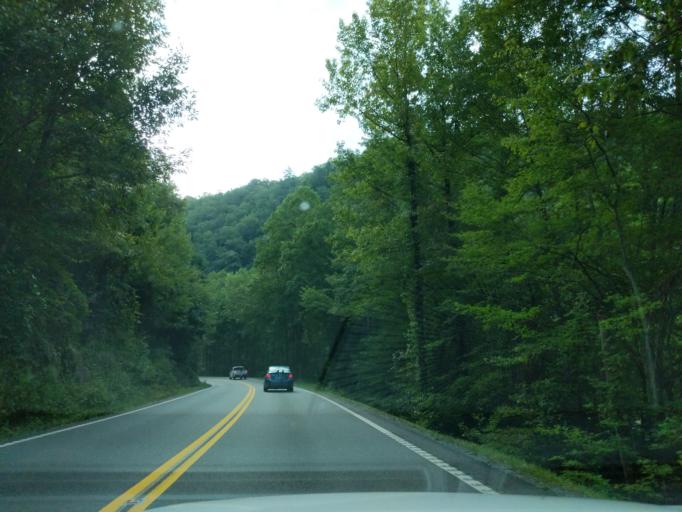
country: US
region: Georgia
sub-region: Fannin County
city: McCaysville
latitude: 35.0741
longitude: -84.5061
